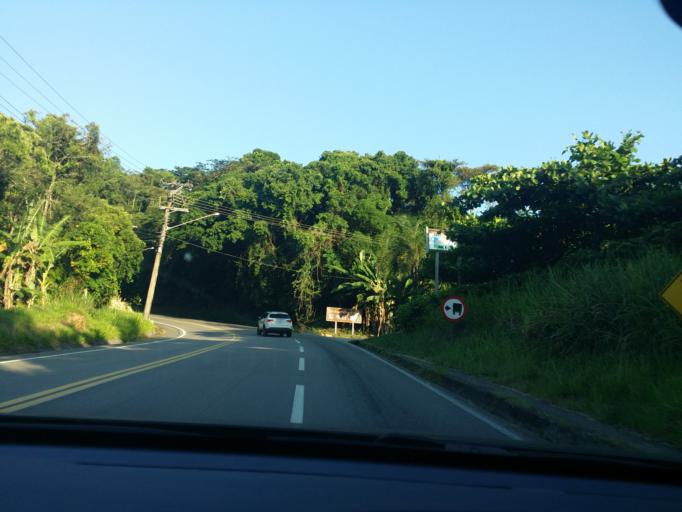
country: BR
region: Sao Paulo
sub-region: Sao Sebastiao
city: Sao Sebastiao
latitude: -23.7830
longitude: -45.6141
